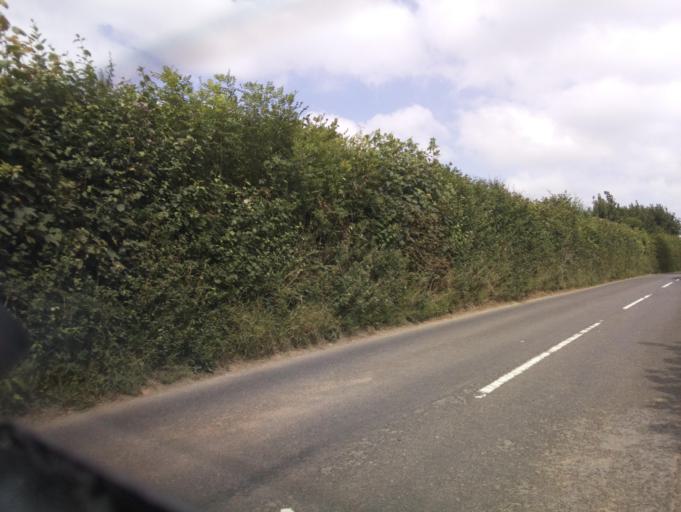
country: GB
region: England
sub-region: Devon
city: South Brent
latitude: 50.4124
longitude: -3.8044
